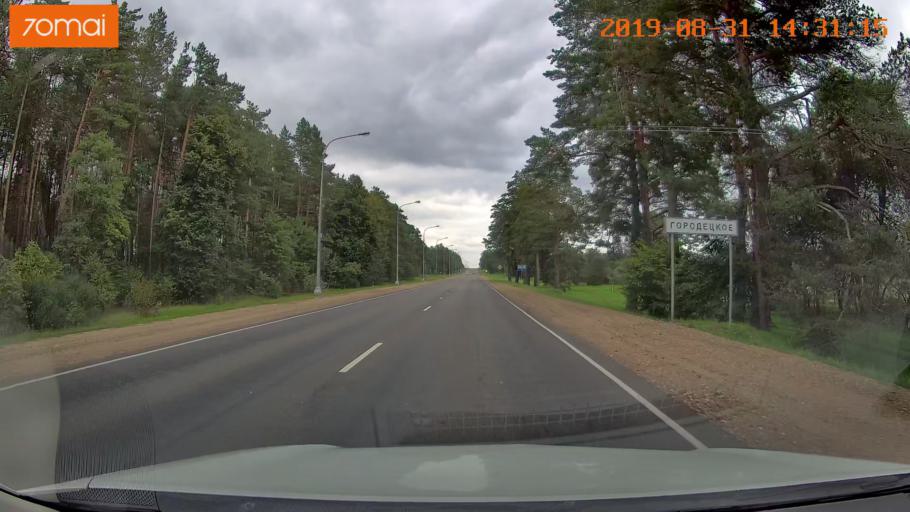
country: RU
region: Smolensk
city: Yekimovichi
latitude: 54.1371
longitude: 33.3694
